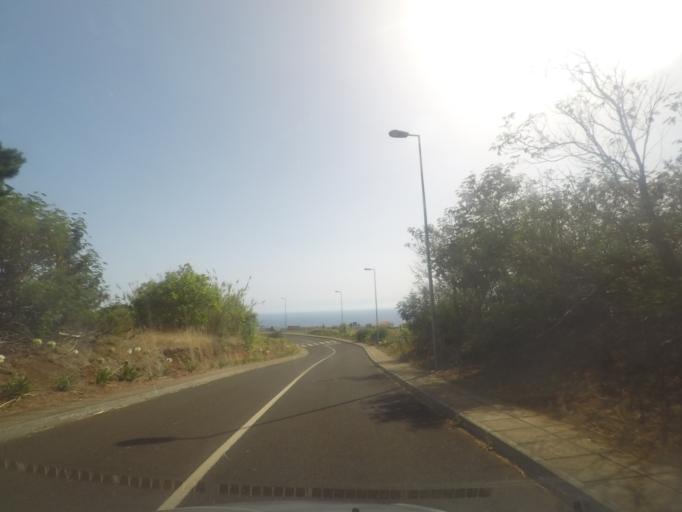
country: PT
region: Madeira
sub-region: Calheta
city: Faja da Ovelha
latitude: 32.8132
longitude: -17.2519
